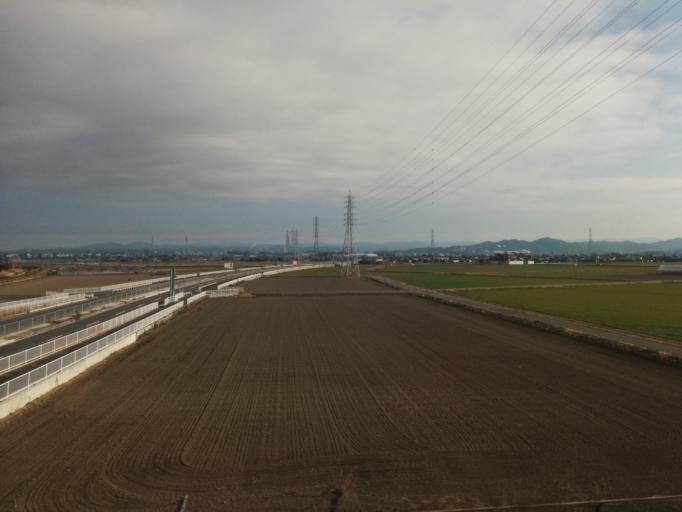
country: JP
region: Aichi
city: Okazaki
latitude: 34.8948
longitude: 137.1287
